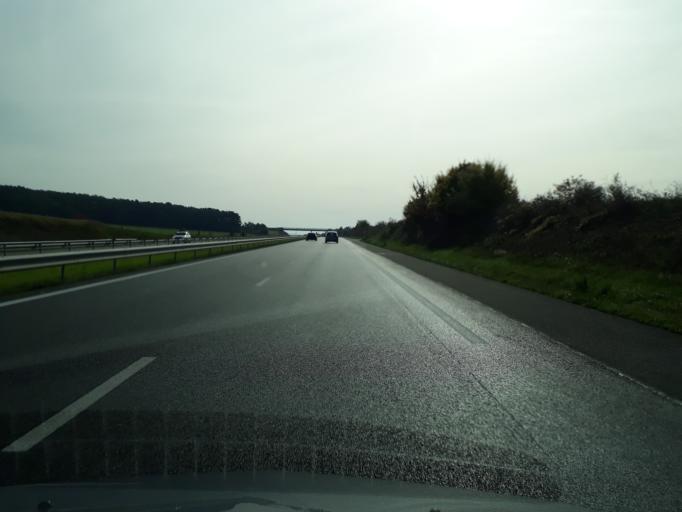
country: FR
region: Bourgogne
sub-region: Departement de l'Yonne
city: Sergines
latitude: 48.3103
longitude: 3.2446
